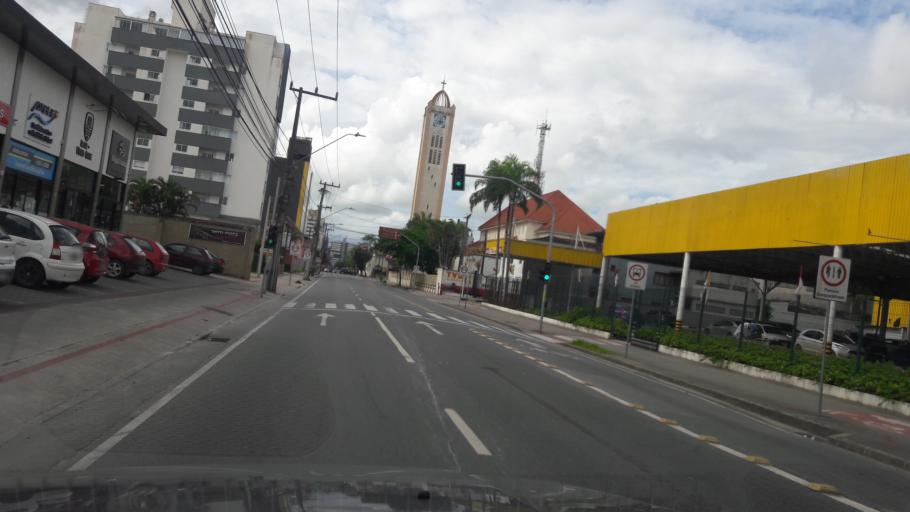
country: BR
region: Santa Catarina
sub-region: Joinville
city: Joinville
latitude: -26.3179
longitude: -48.8426
